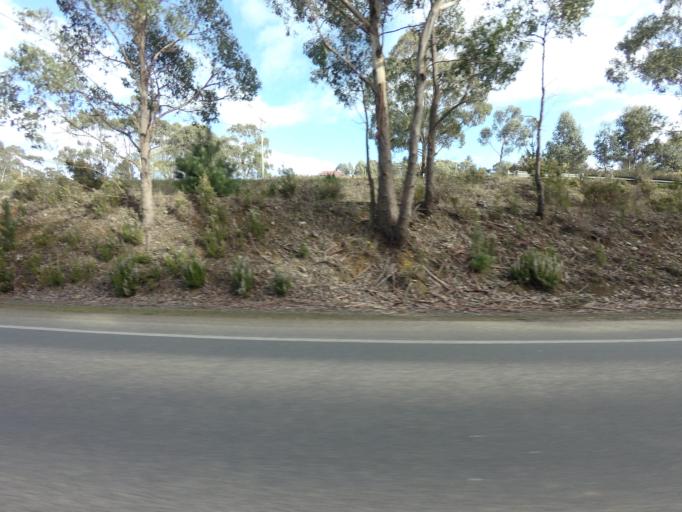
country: AU
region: Tasmania
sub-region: Huon Valley
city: Geeveston
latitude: -43.1611
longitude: 146.9516
